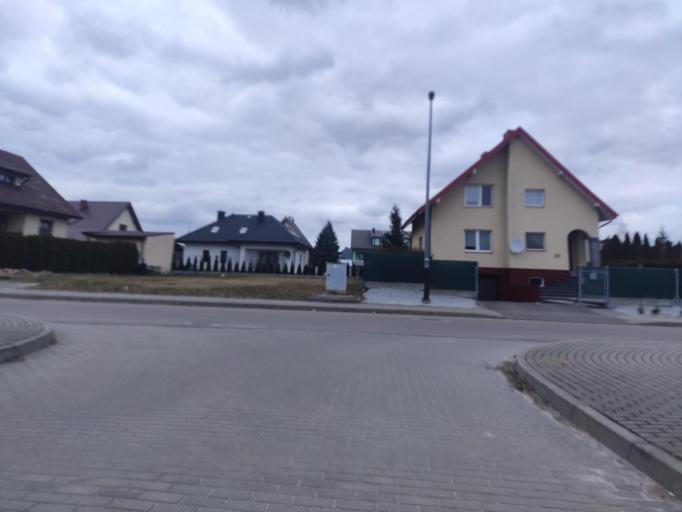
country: PL
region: Lublin Voivodeship
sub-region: Powiat lubartowski
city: Kock
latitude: 51.6404
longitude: 22.4326
